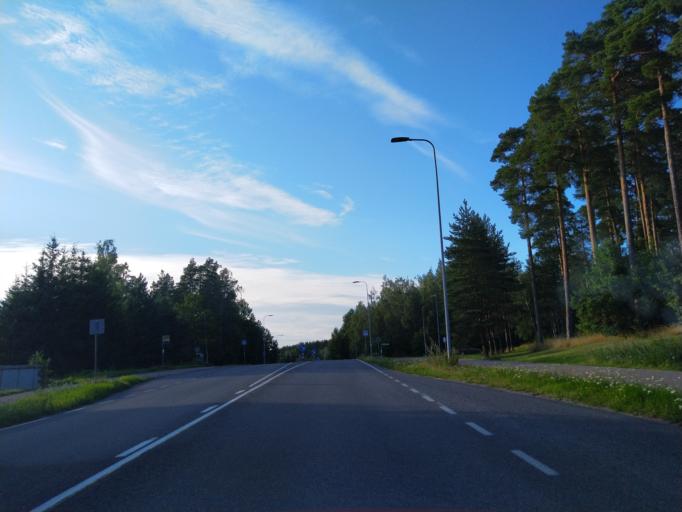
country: FI
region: Varsinais-Suomi
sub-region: Turku
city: Kaarina
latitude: 60.4110
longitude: 22.3135
